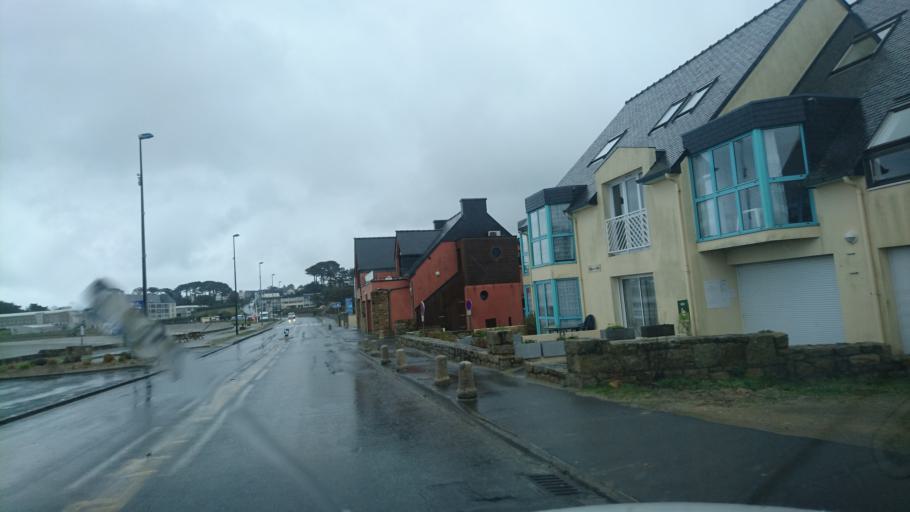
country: FR
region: Brittany
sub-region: Departement des Cotes-d'Armor
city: Trevou-Treguignec
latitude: 48.8190
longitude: -3.3554
